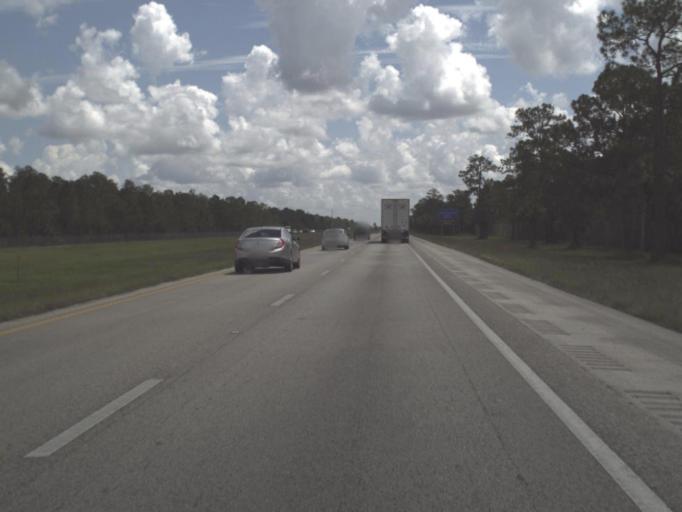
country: US
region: Florida
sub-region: Collier County
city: Orangetree
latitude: 26.1530
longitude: -81.4757
